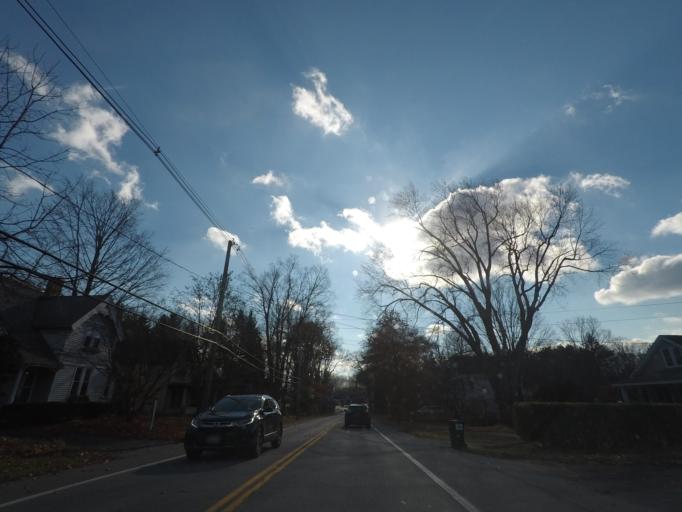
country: US
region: New York
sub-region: Schenectady County
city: East Glenville
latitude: 42.9061
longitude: -73.8963
